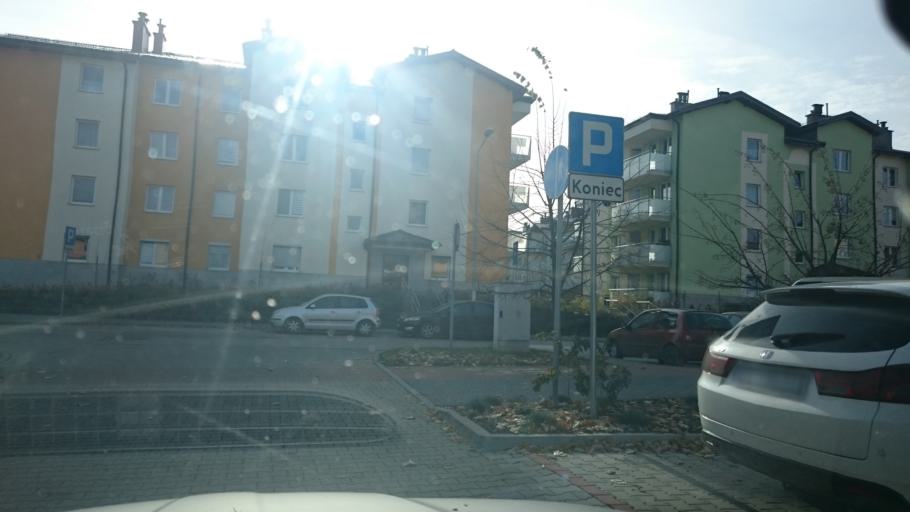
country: PL
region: Lesser Poland Voivodeship
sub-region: Powiat wielicki
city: Czarnochowice
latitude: 50.0201
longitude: 20.0549
